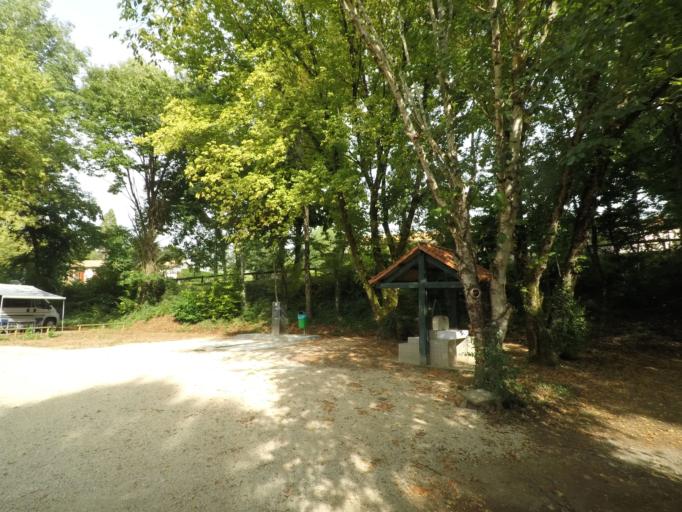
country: FR
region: Poitou-Charentes
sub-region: Departement des Deux-Sevres
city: Melle
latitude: 46.2312
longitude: -0.1444
